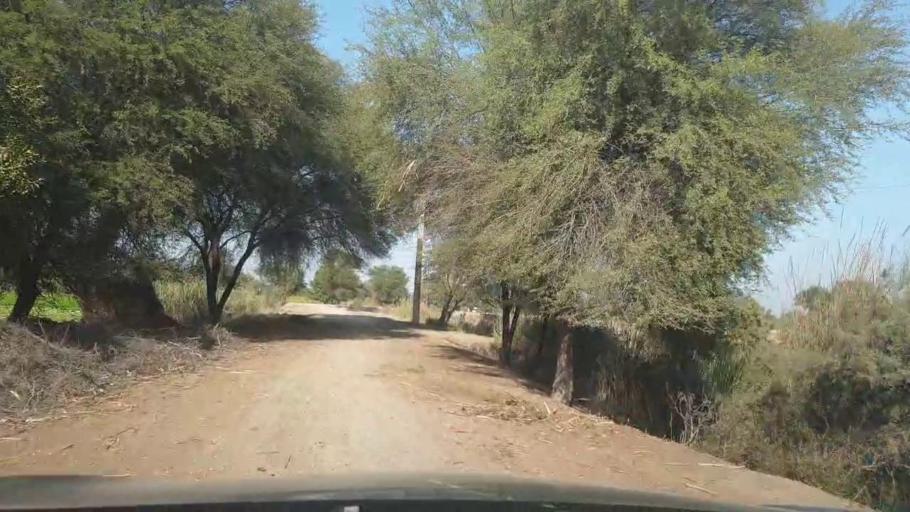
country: PK
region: Sindh
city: Khairpur
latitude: 28.1426
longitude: 69.5973
